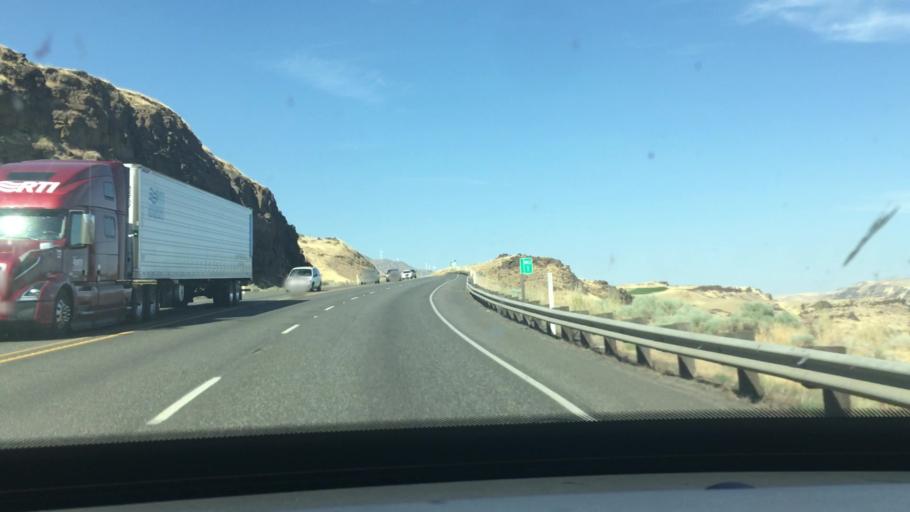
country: US
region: Washington
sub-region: Klickitat County
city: Goldendale
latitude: 45.6882
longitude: -120.8235
